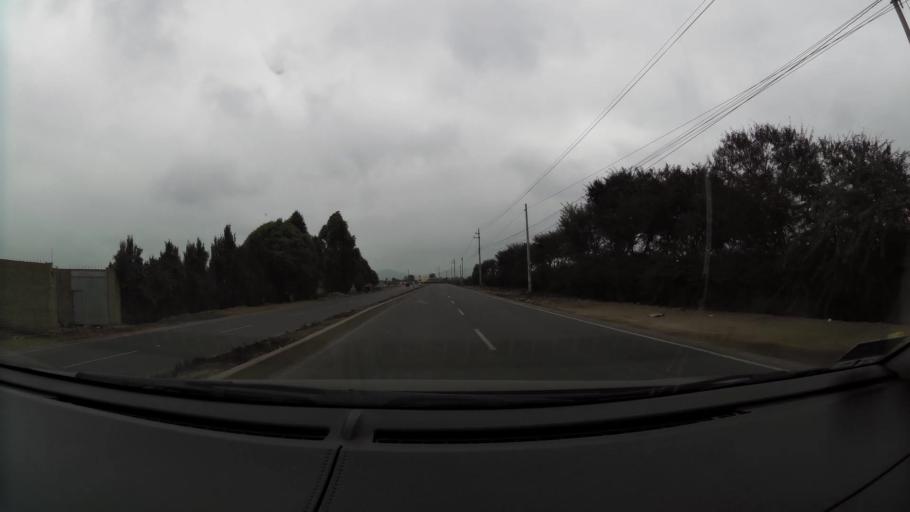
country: PE
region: Lima
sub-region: Provincia de Huaral
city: Huaral
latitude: -11.5146
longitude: -77.2359
